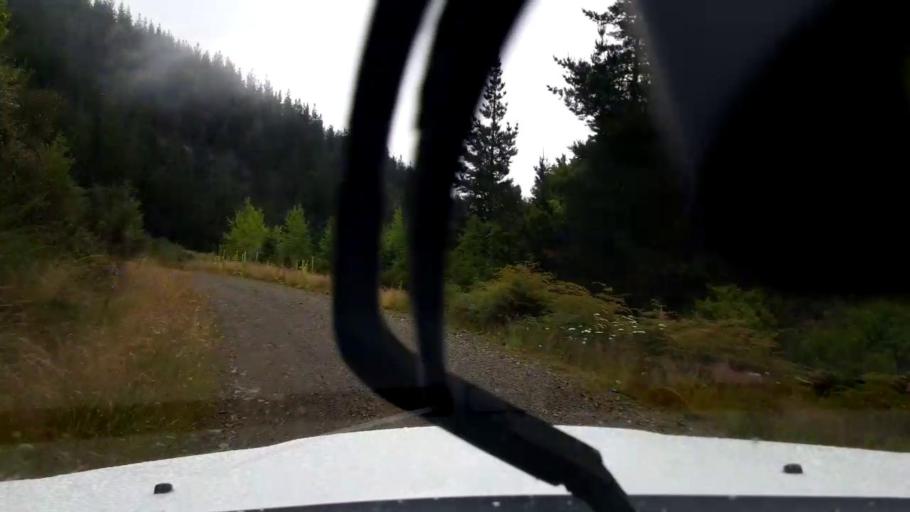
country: NZ
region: Canterbury
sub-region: Timaru District
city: Pleasant Point
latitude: -44.0333
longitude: 171.0050
